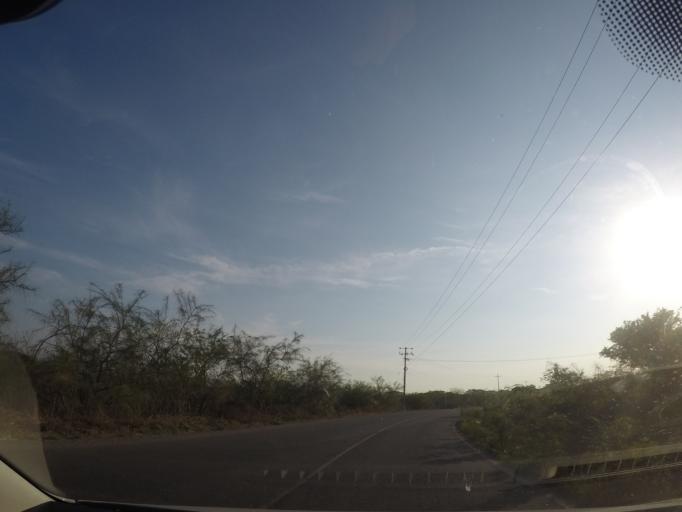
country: MX
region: Oaxaca
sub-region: Santo Domingo Tehuantepec
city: La Noria
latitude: 16.2294
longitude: -95.1851
